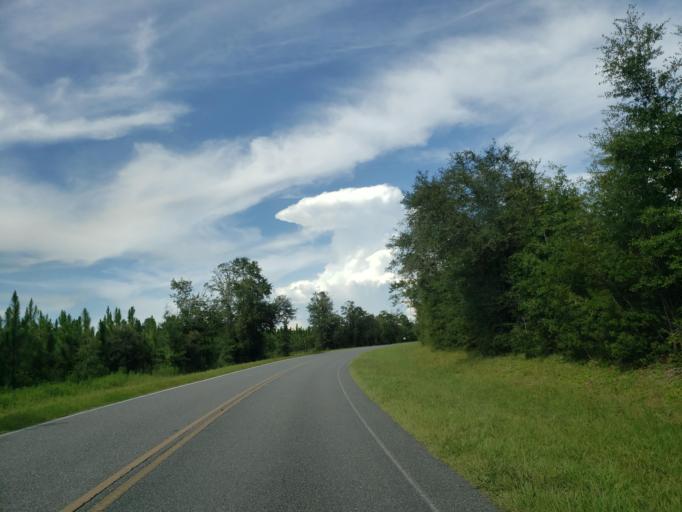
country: US
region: Georgia
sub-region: Echols County
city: Statenville
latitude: 30.6160
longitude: -83.2168
